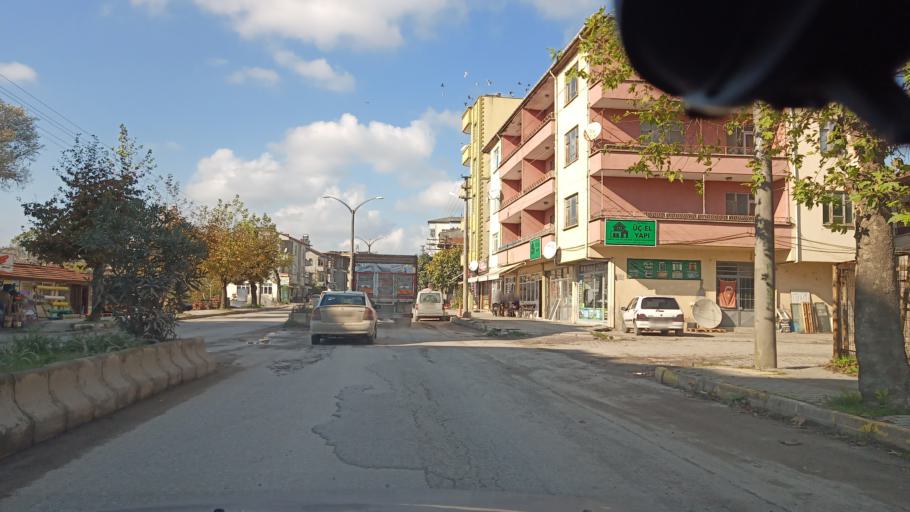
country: TR
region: Sakarya
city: Kaynarca
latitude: 41.0376
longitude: 30.2984
